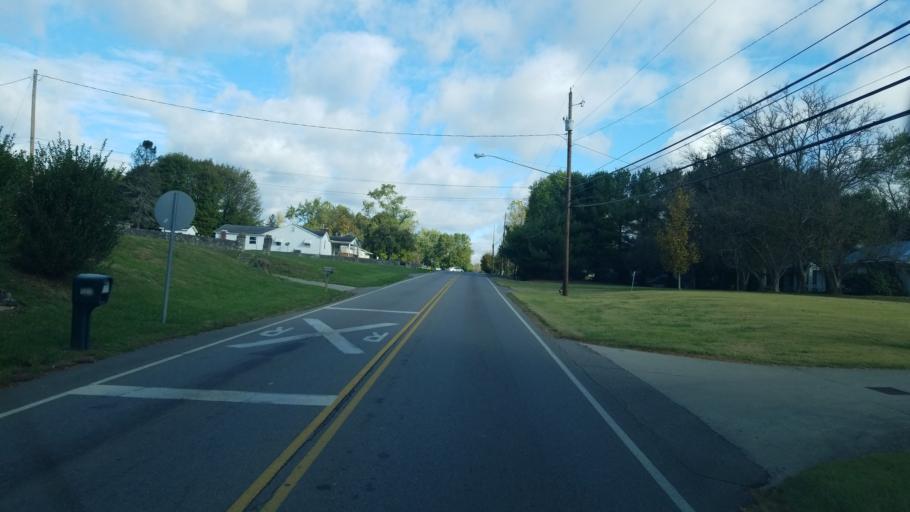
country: US
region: Ohio
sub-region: Jackson County
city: Wellston
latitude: 39.1349
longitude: -82.5297
